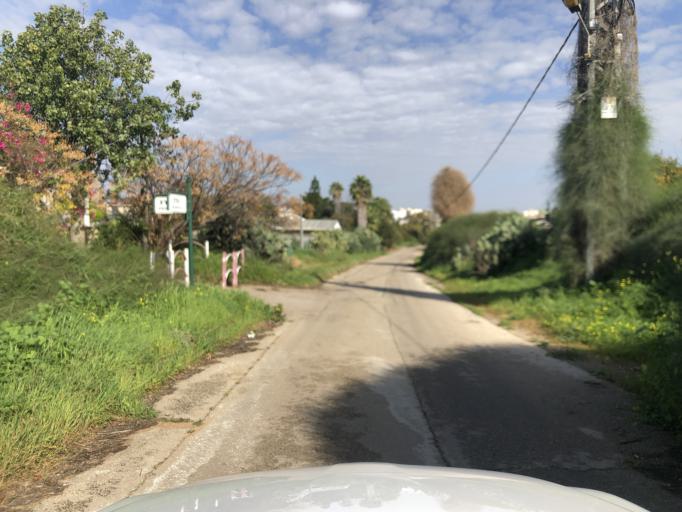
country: IL
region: Central District
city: Ness Ziona
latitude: 31.9164
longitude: 34.7963
